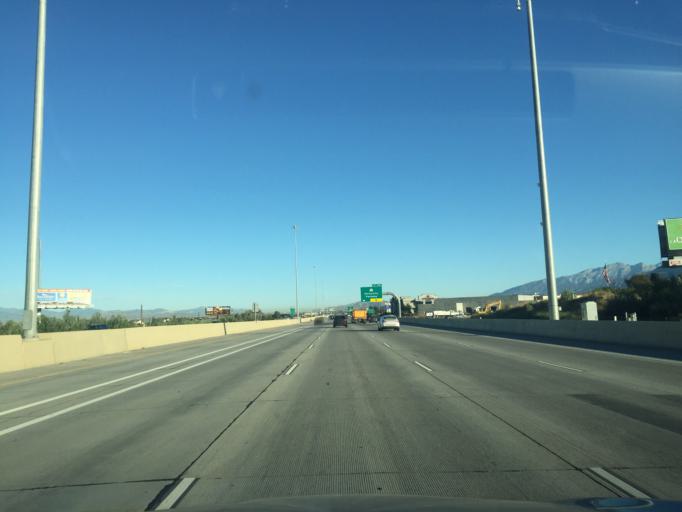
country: US
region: Utah
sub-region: Utah County
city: Orem
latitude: 40.2664
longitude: -111.7111
